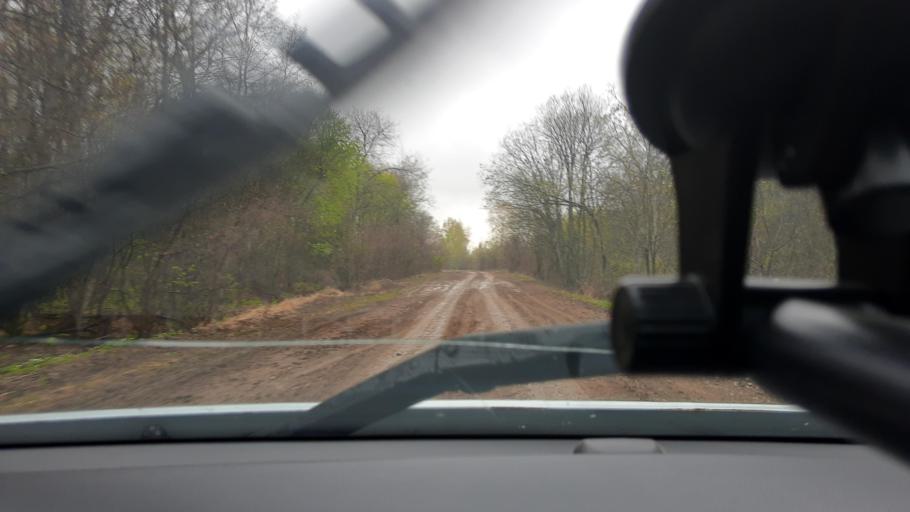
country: RU
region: Bashkortostan
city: Pavlovka
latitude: 55.4294
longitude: 56.3494
